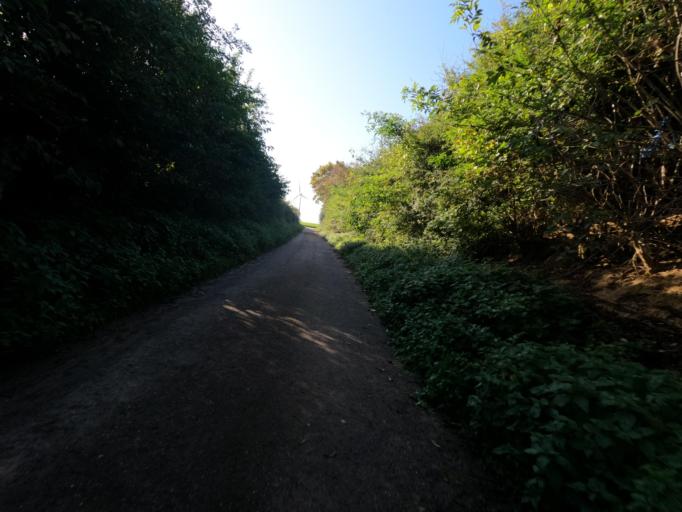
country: DE
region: North Rhine-Westphalia
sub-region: Regierungsbezirk Koln
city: Linnich
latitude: 50.9945
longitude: 6.2405
